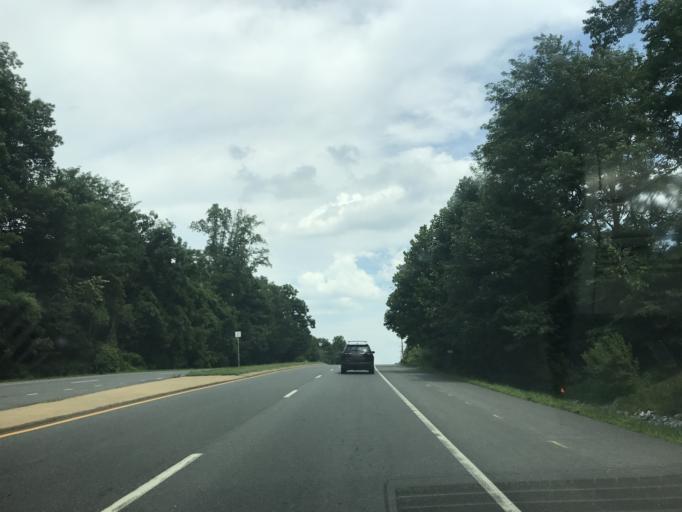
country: US
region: Delaware
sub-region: New Castle County
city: Greenville
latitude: 39.7629
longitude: -75.6321
